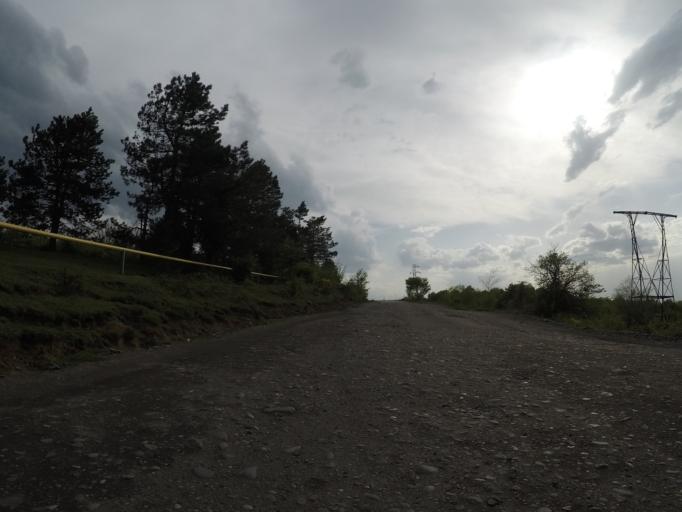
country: GE
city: Shorapani
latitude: 42.1770
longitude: 43.1335
